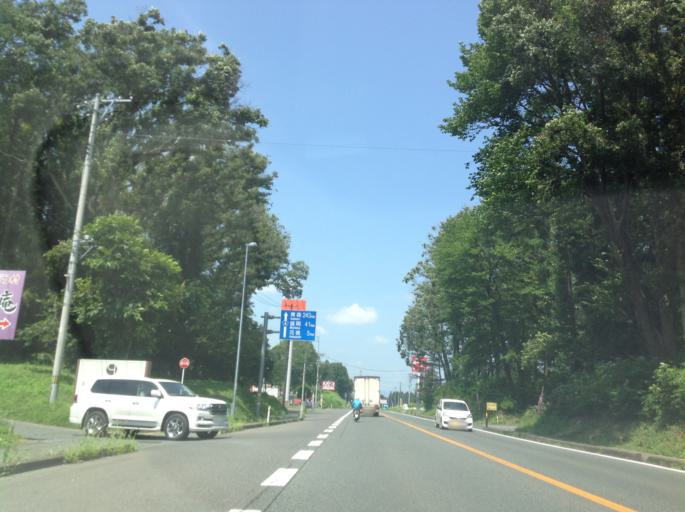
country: JP
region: Iwate
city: Hanamaki
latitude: 39.3408
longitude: 141.1078
